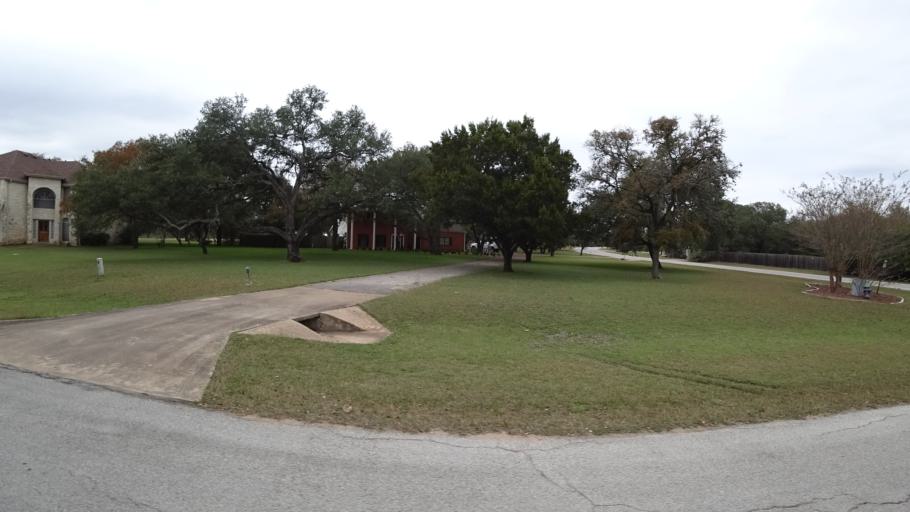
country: US
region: Texas
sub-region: Travis County
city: Shady Hollow
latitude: 30.1576
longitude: -97.8728
